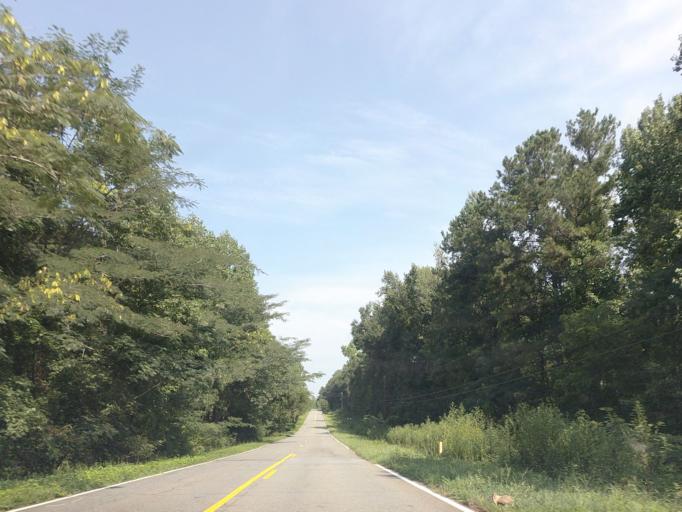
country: US
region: Georgia
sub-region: Bibb County
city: Macon
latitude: 32.9099
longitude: -83.6935
